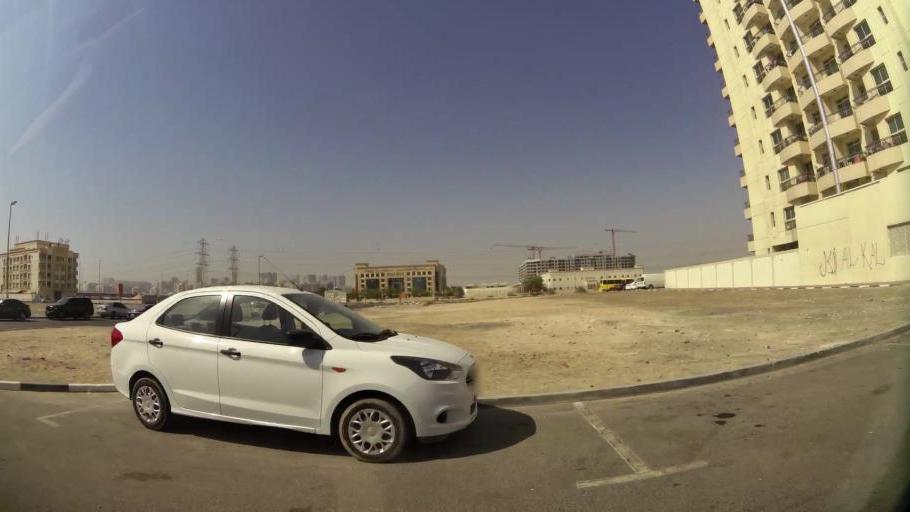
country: AE
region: Ash Shariqah
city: Sharjah
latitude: 25.2773
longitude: 55.3770
